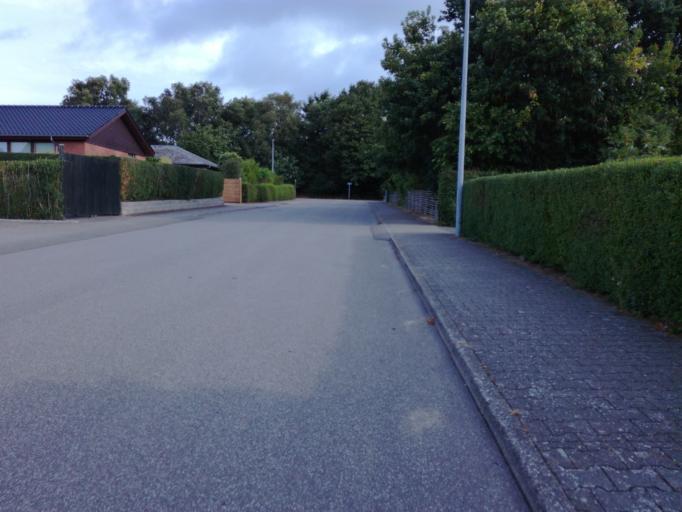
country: DK
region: South Denmark
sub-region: Fredericia Kommune
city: Fredericia
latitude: 55.5822
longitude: 9.7857
